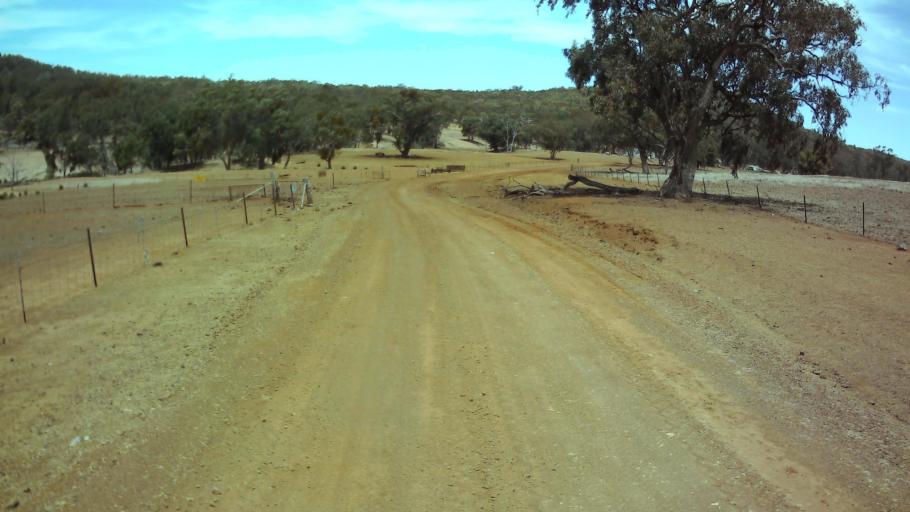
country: AU
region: New South Wales
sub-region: Weddin
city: Grenfell
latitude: -33.7902
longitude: 148.1581
